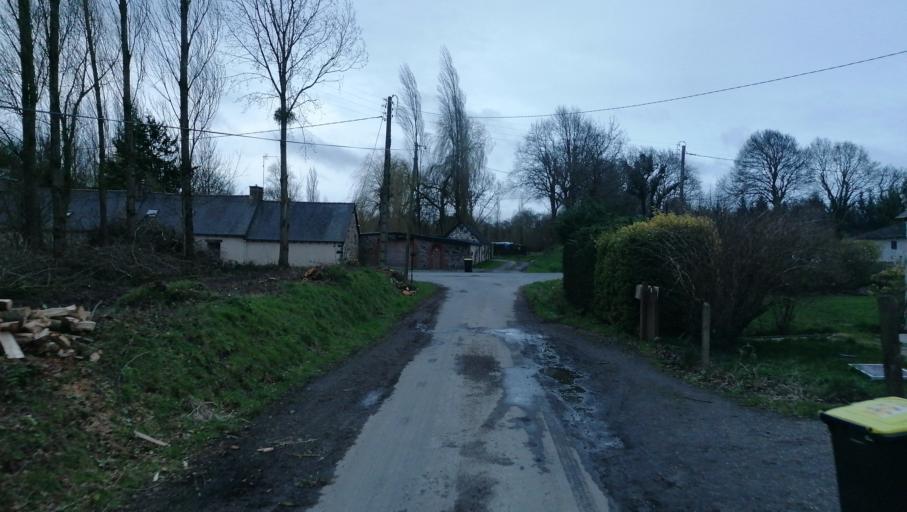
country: FR
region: Brittany
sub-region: Departement des Cotes-d'Armor
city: Goudelin
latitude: 48.5746
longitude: -3.0522
